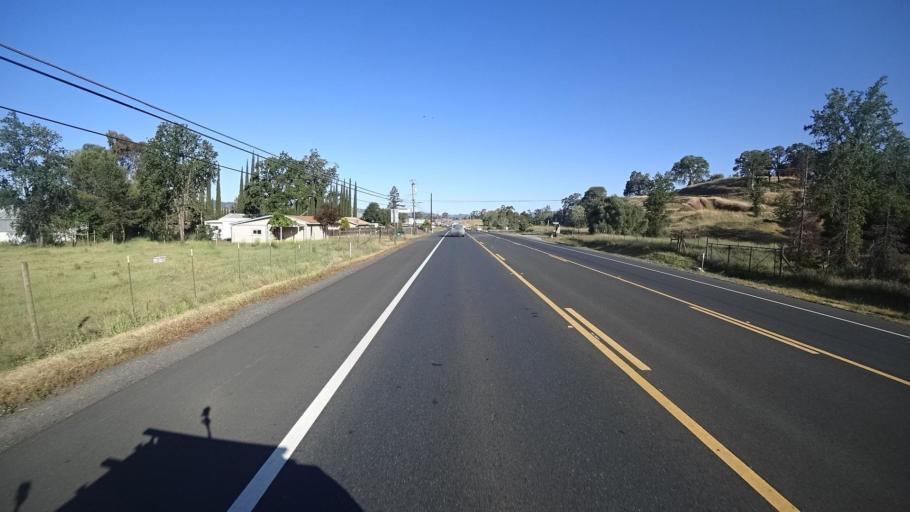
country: US
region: California
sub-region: Lake County
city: Nice
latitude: 39.1283
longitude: -122.8669
